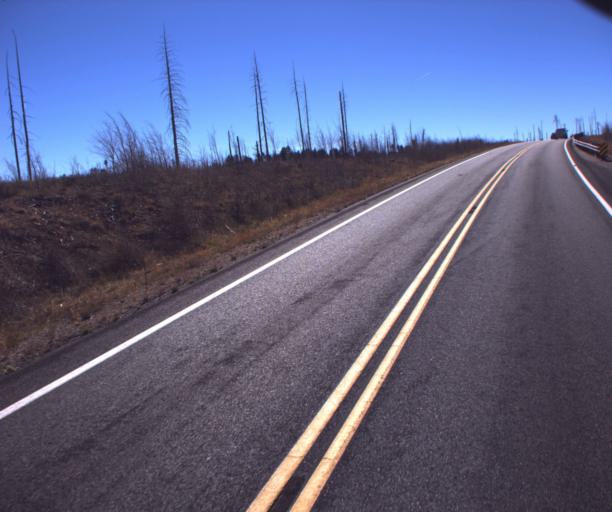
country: US
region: Arizona
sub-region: Coconino County
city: Fredonia
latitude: 36.6105
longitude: -112.1852
